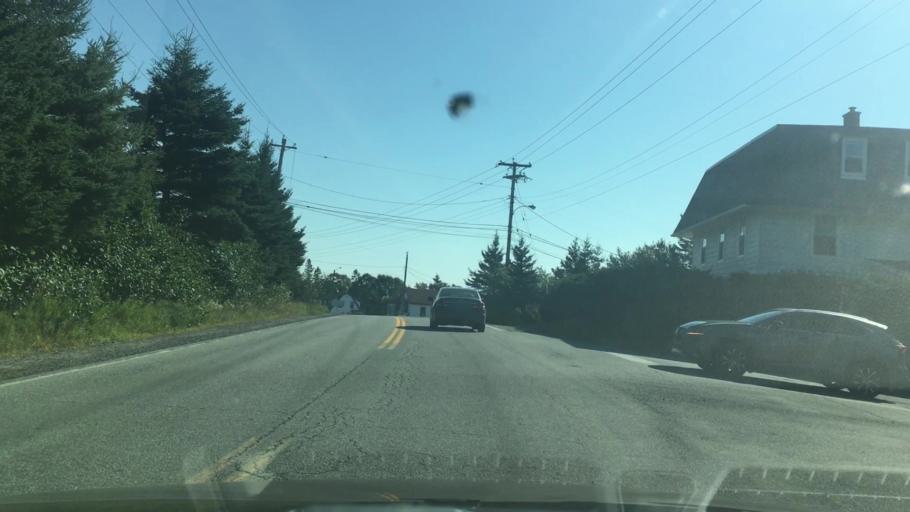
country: CA
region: Nova Scotia
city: Cole Harbour
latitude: 44.7831
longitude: -63.1550
